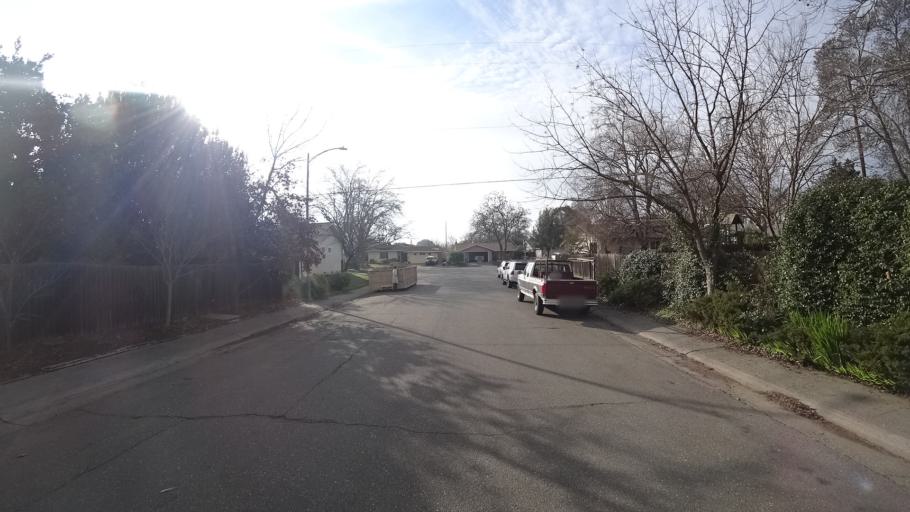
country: US
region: California
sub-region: Yolo County
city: Davis
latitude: 38.5575
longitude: -121.7237
